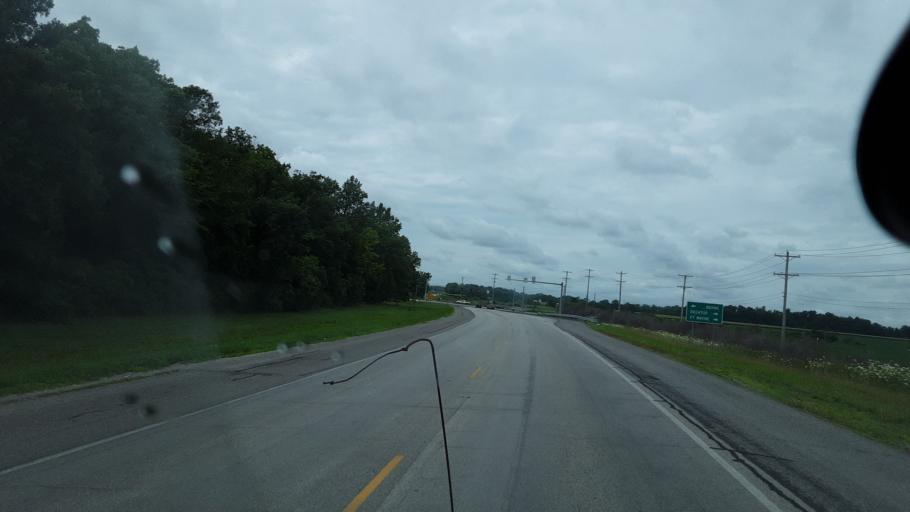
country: US
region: Indiana
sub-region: Adams County
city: Decatur
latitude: 40.8033
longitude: -84.9335
